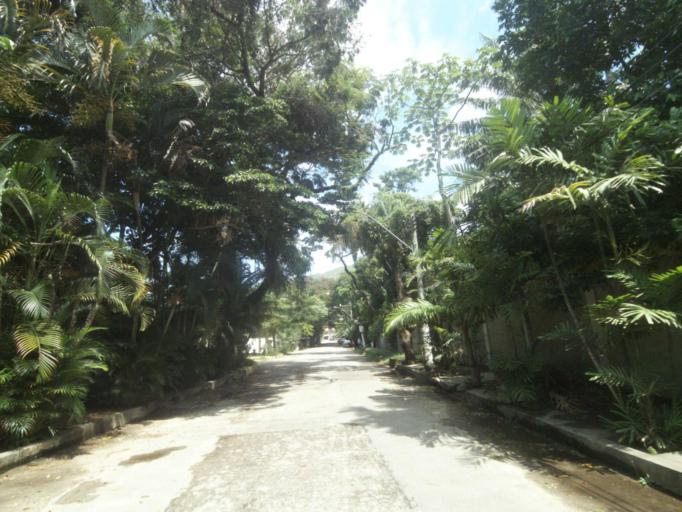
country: BR
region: Rio de Janeiro
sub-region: Niteroi
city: Niteroi
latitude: -22.9725
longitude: -43.0367
